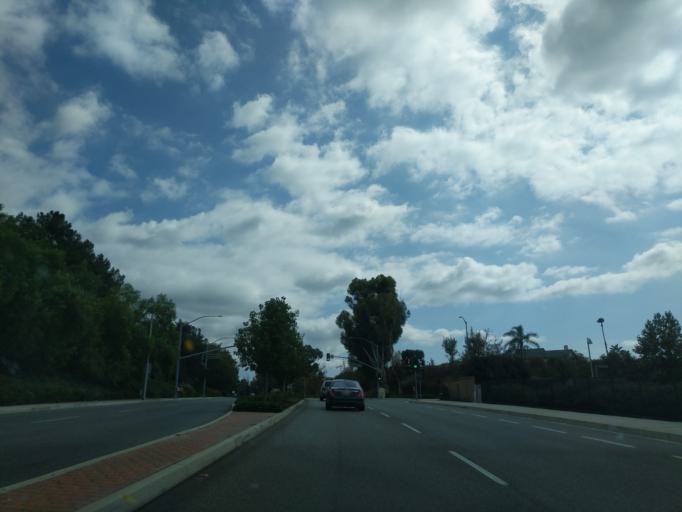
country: US
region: California
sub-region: Orange County
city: Portola Hills
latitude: 33.6508
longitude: -117.6445
